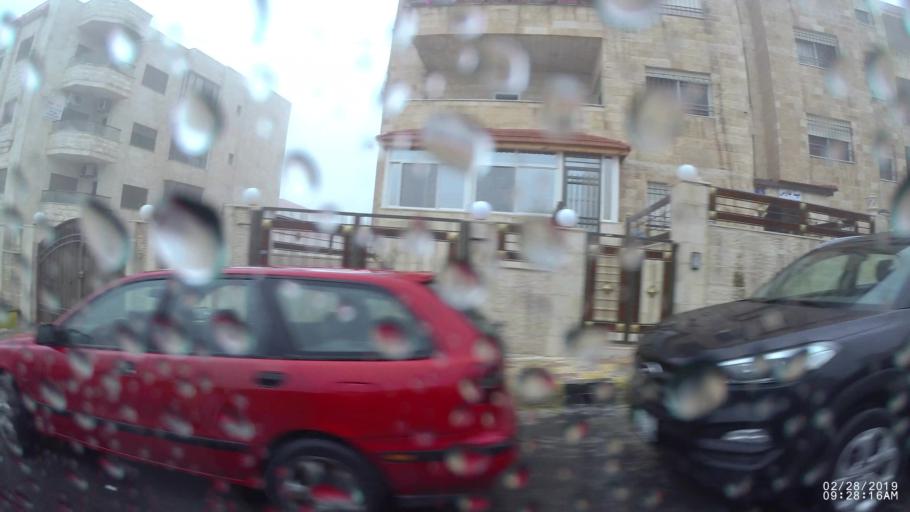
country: JO
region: Amman
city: Al Jubayhah
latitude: 32.0058
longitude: 35.8830
